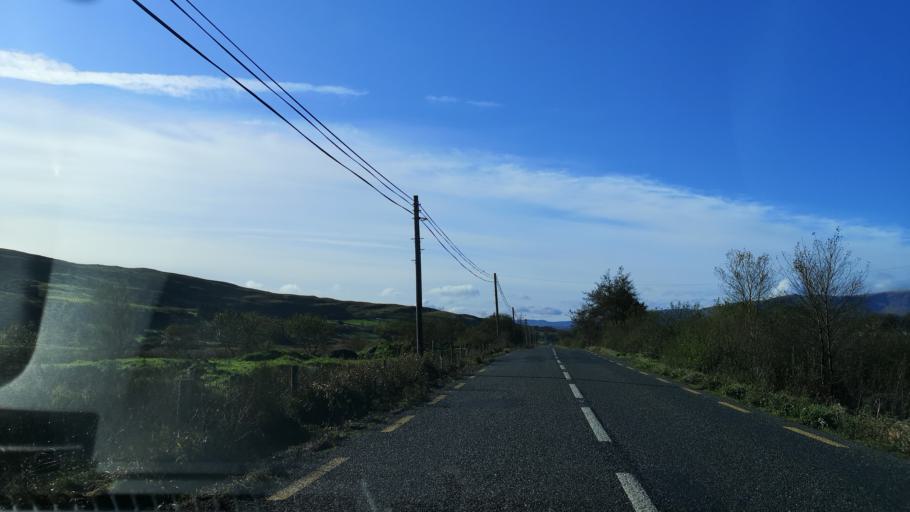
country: IE
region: Connaught
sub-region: Maigh Eo
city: Westport
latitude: 53.7183
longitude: -9.5439
